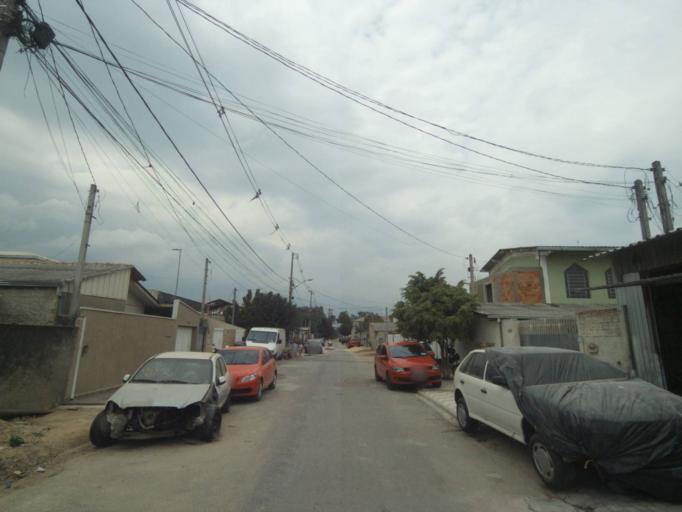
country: BR
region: Parana
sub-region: Sao Jose Dos Pinhais
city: Sao Jose dos Pinhais
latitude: -25.4978
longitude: -49.2035
